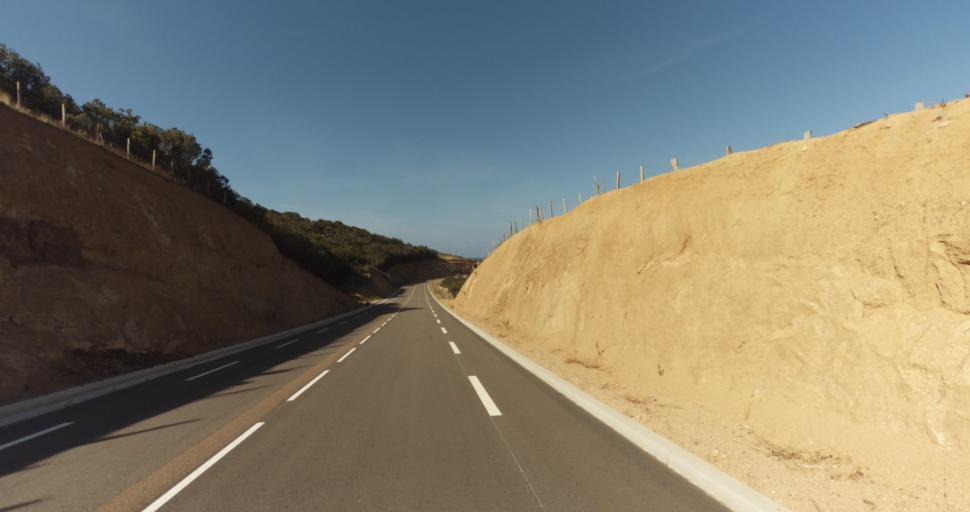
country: FR
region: Corsica
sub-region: Departement de la Corse-du-Sud
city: Ajaccio
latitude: 41.9308
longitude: 8.6590
